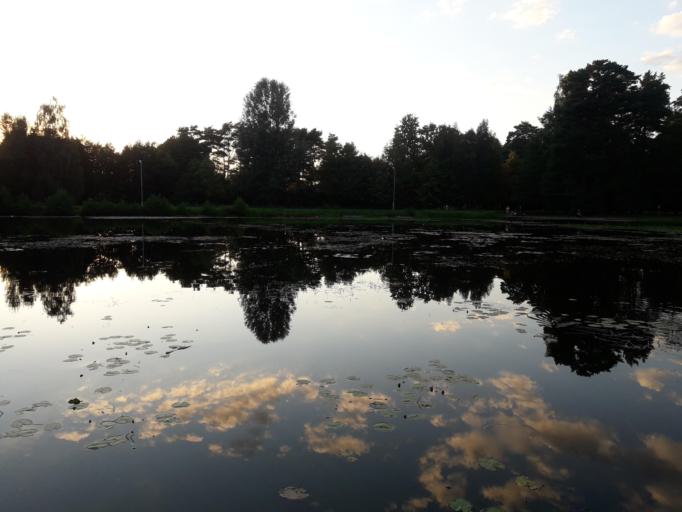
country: LT
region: Alytaus apskritis
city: Druskininkai
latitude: 54.0186
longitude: 24.0111
